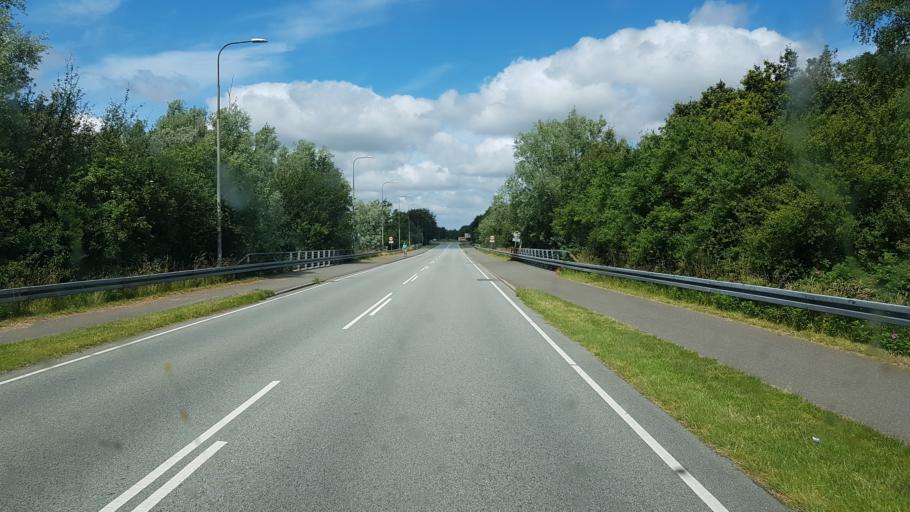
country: DK
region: South Denmark
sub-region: Billund Kommune
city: Grindsted
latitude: 55.7571
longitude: 8.9027
